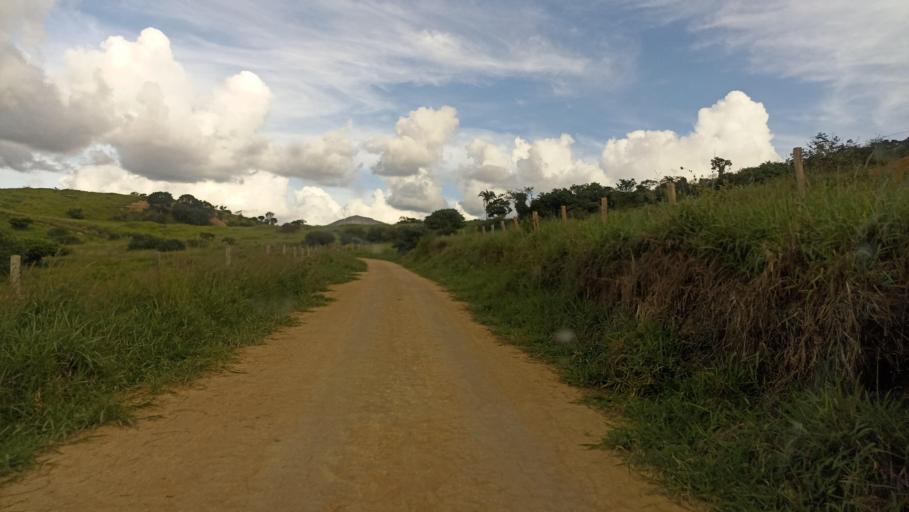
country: BR
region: Minas Gerais
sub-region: Almenara
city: Almenara
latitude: -16.5485
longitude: -40.4530
